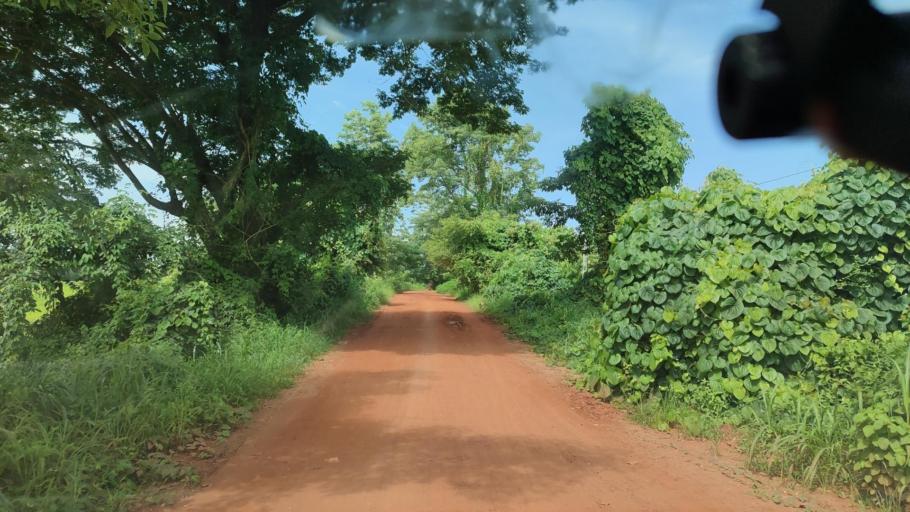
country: MM
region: Ayeyarwady
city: Hinthada
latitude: 17.6880
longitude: 95.4989
